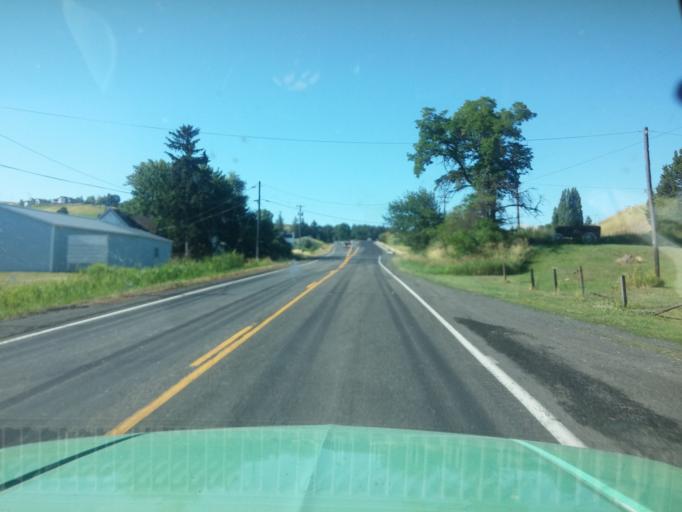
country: US
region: Idaho
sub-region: Latah County
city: Moscow
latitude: 46.6998
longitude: -117.0072
